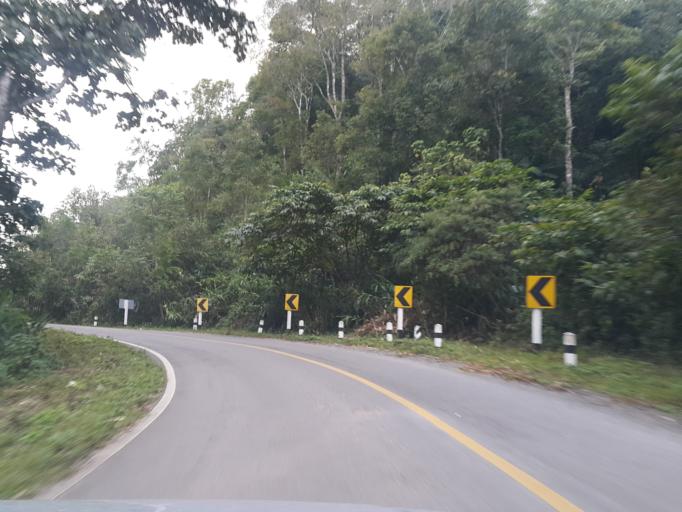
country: TH
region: Mae Hong Son
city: Khun Yuam
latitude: 18.7959
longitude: 98.0885
